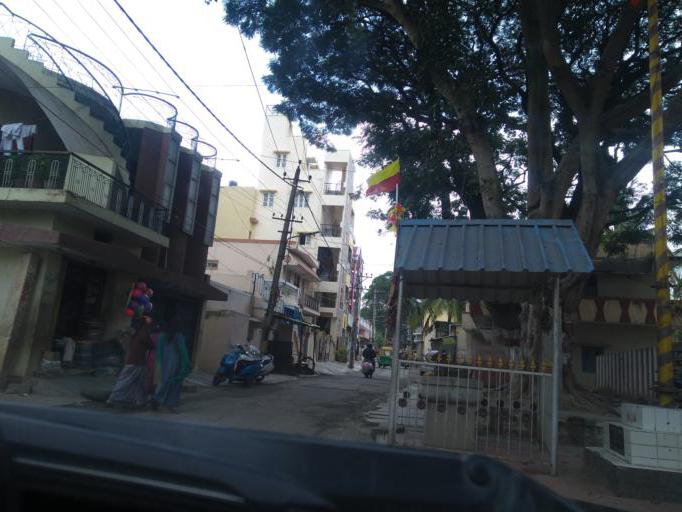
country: IN
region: Karnataka
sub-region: Bangalore Urban
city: Bangalore
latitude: 13.0098
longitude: 77.6593
